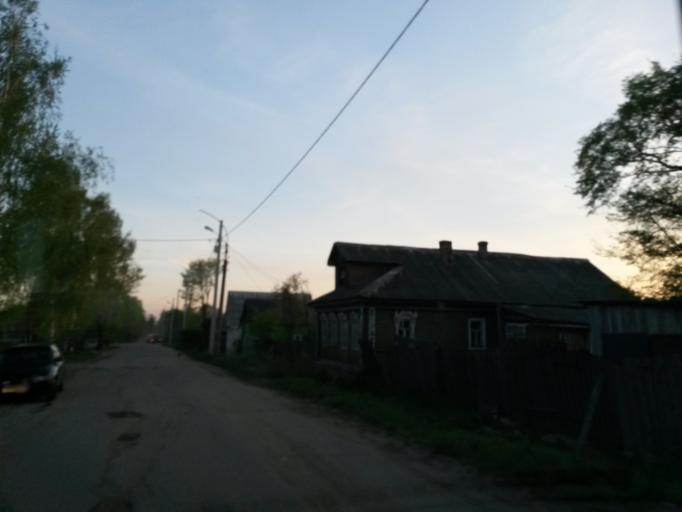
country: RU
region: Jaroslavl
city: Tutayev
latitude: 57.8867
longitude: 39.5509
